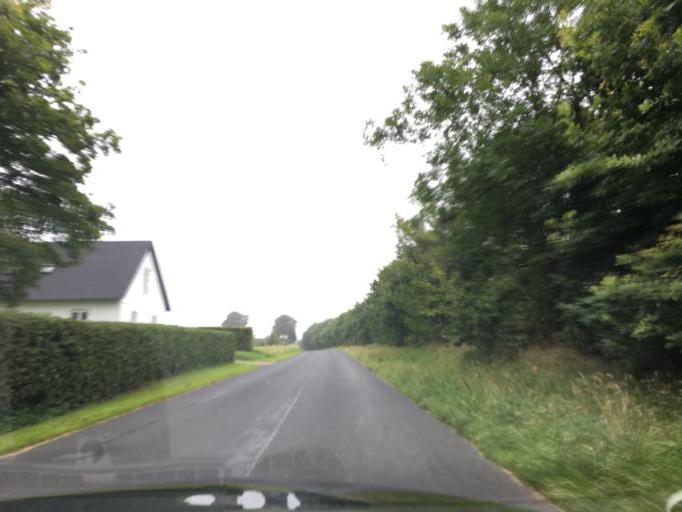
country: DK
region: South Denmark
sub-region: Kolding Kommune
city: Kolding
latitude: 55.5593
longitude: 9.4421
